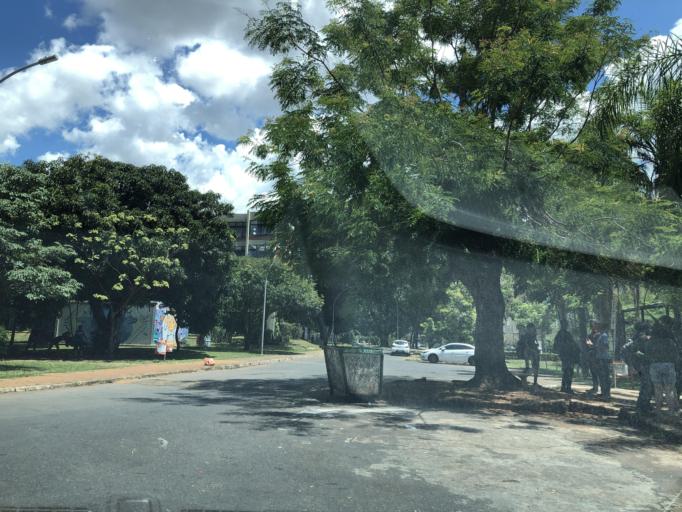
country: BR
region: Federal District
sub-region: Brasilia
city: Brasilia
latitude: -15.7552
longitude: -47.8813
